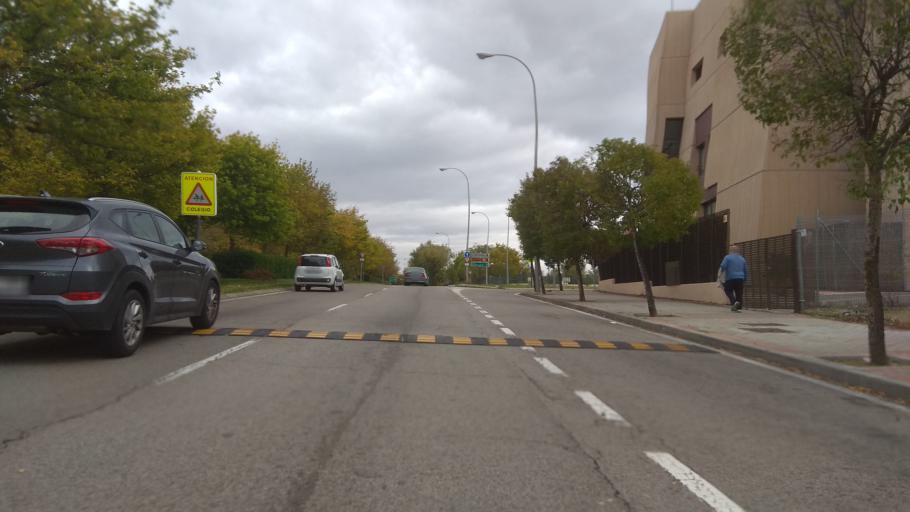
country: ES
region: Madrid
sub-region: Provincia de Madrid
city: Vicalvaro
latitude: 40.4057
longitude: -3.6204
